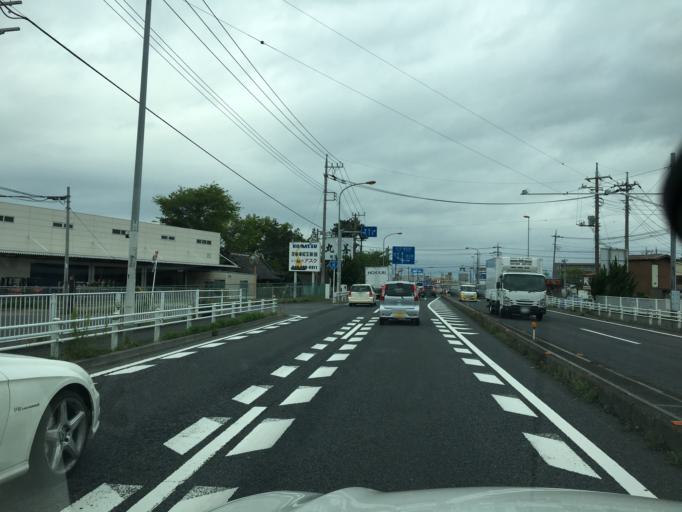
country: JP
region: Saitama
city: Koshigaya
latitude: 35.8624
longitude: 139.7805
